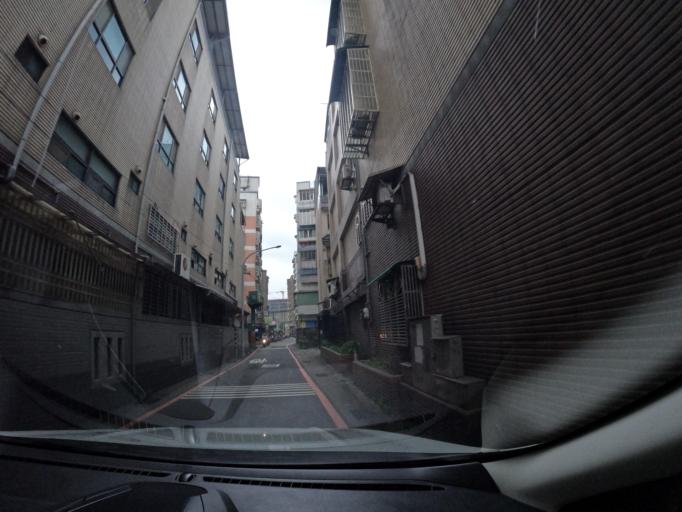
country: TW
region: Taipei
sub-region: Taipei
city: Banqiao
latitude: 24.9657
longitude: 121.4201
